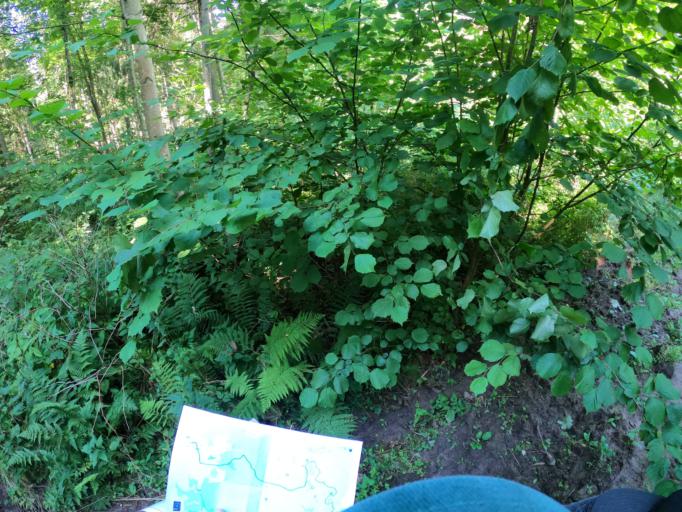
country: LT
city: Tytuveneliai
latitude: 55.7997
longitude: 23.0899
